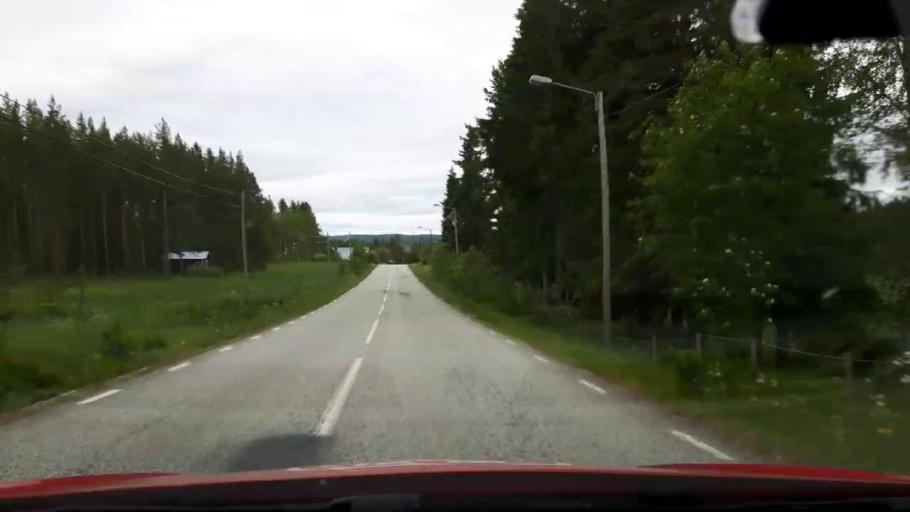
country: SE
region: Jaemtland
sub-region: Stroemsunds Kommun
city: Stroemsund
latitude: 63.3378
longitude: 15.7640
